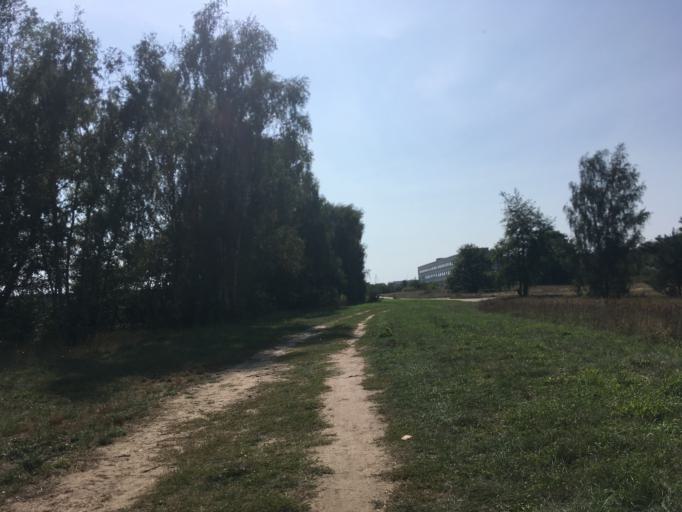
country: DE
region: Brandenburg
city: Erkner
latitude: 52.3995
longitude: 13.7237
